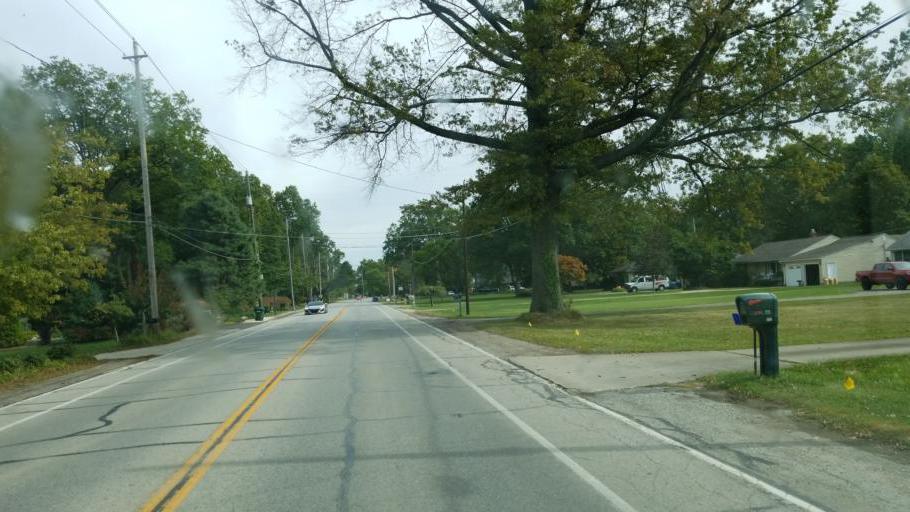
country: US
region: Ohio
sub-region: Cuyahoga County
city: Bay Village
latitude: 41.5054
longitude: -81.9729
